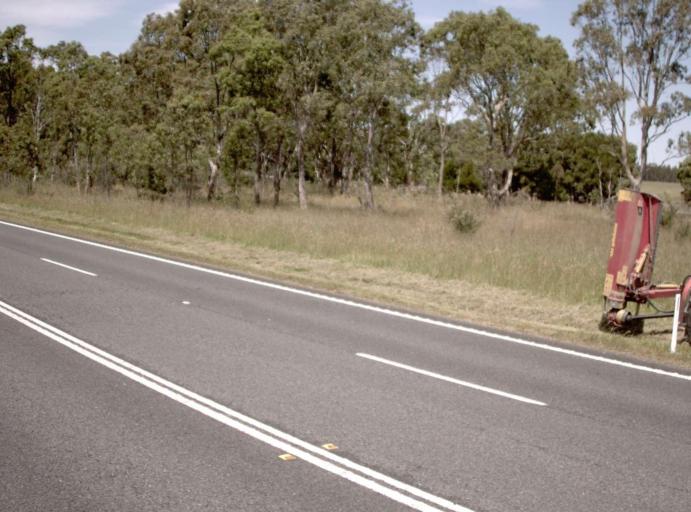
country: AU
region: Victoria
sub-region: Latrobe
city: Traralgon
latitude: -38.1779
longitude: 146.6351
